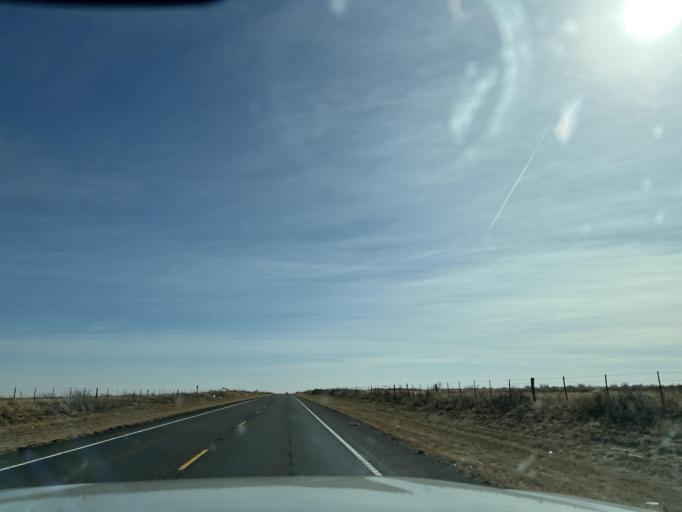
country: US
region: Texas
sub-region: Andrews County
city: Andrews
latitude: 32.4670
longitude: -102.4608
